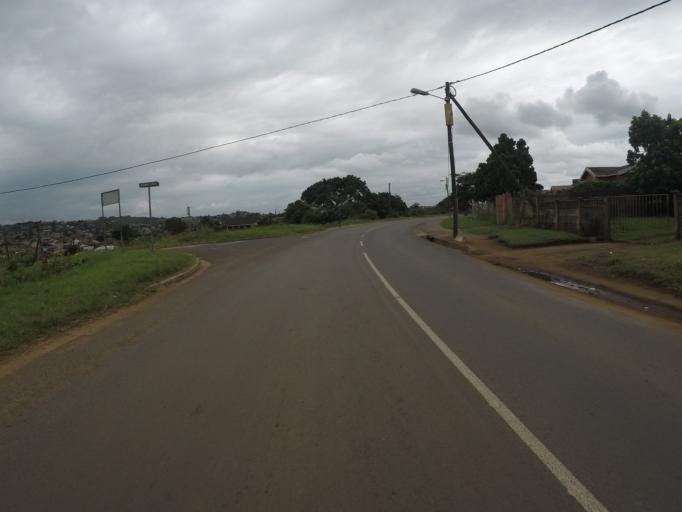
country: ZA
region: KwaZulu-Natal
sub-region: uThungulu District Municipality
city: Empangeni
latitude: -28.7834
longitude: 31.8546
